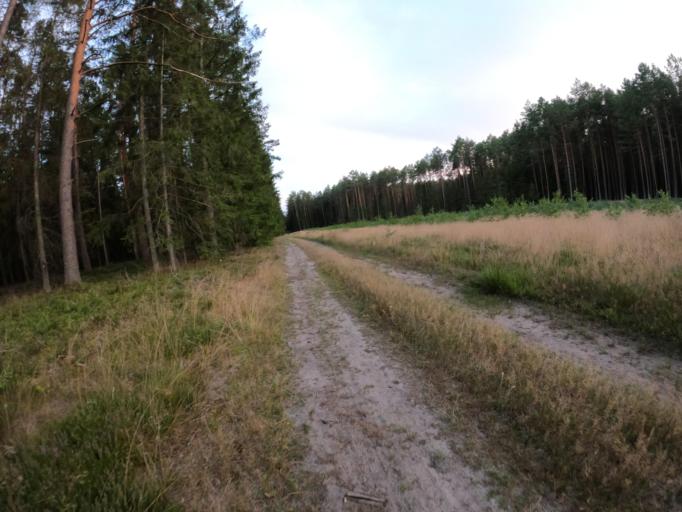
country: PL
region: West Pomeranian Voivodeship
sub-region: Powiat koszalinski
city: Sianow
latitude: 54.0973
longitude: 16.4106
